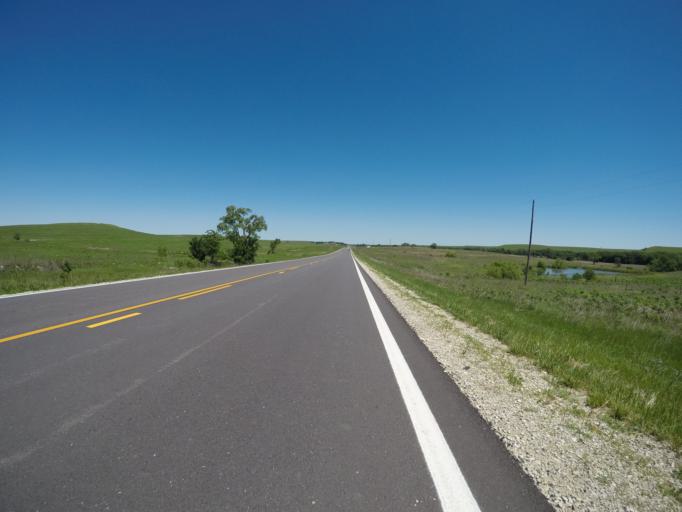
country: US
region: Kansas
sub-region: Chase County
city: Cottonwood Falls
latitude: 38.4113
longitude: -96.5570
